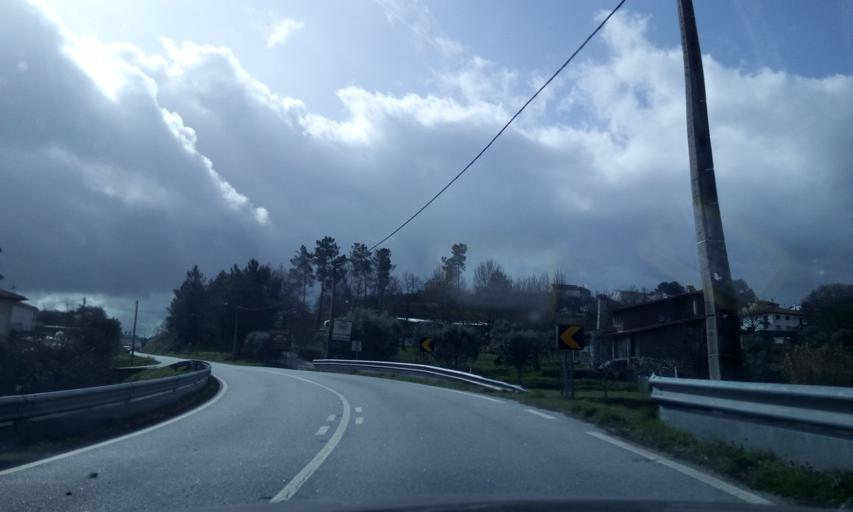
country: PT
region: Viseu
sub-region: Mangualde
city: Mangualde
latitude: 40.6266
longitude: -7.7538
